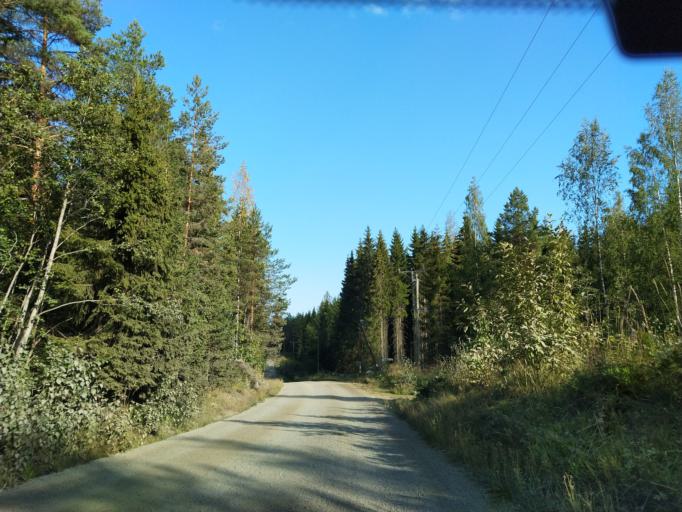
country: FI
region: Central Finland
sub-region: Jaemsae
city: Kuhmoinen
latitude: 61.6910
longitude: 24.9537
